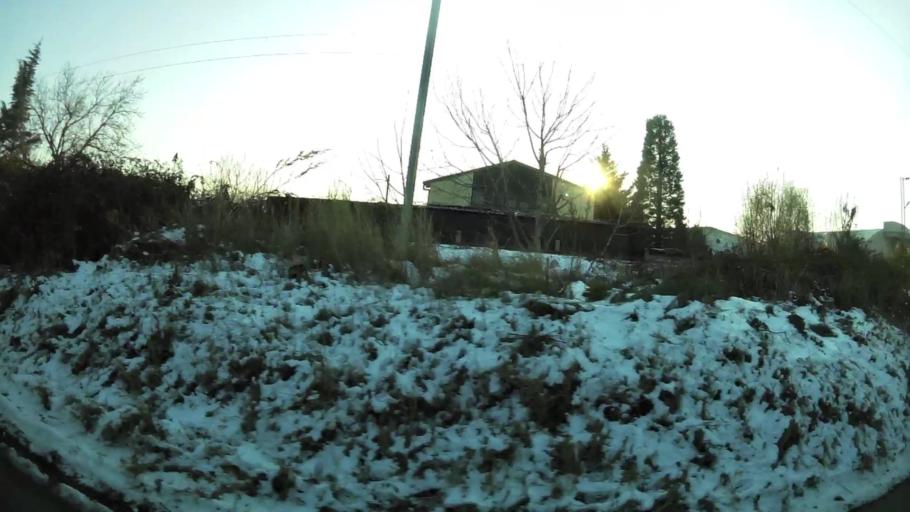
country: MK
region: Kisela Voda
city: Usje
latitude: 41.9724
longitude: 21.4682
